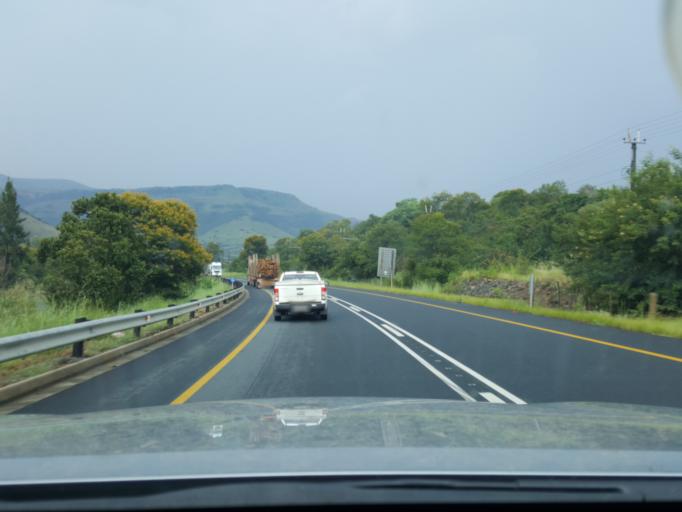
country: ZA
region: Mpumalanga
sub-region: Nkangala District Municipality
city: Belfast
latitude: -25.6318
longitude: 30.3958
